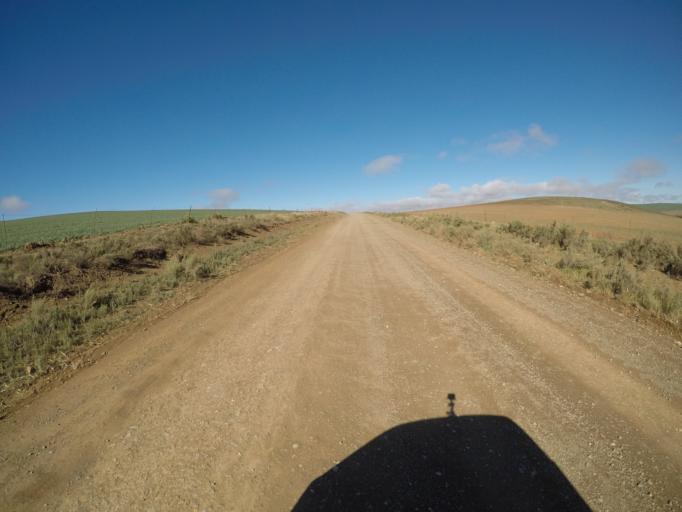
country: ZA
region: Western Cape
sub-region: Overberg District Municipality
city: Caledon
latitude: -34.1127
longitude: 19.7098
